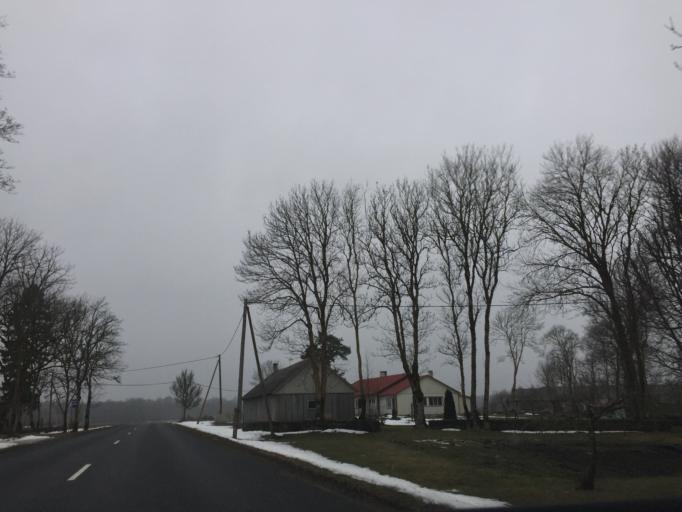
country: EE
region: Saare
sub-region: Orissaare vald
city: Orissaare
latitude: 58.3921
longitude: 22.8425
